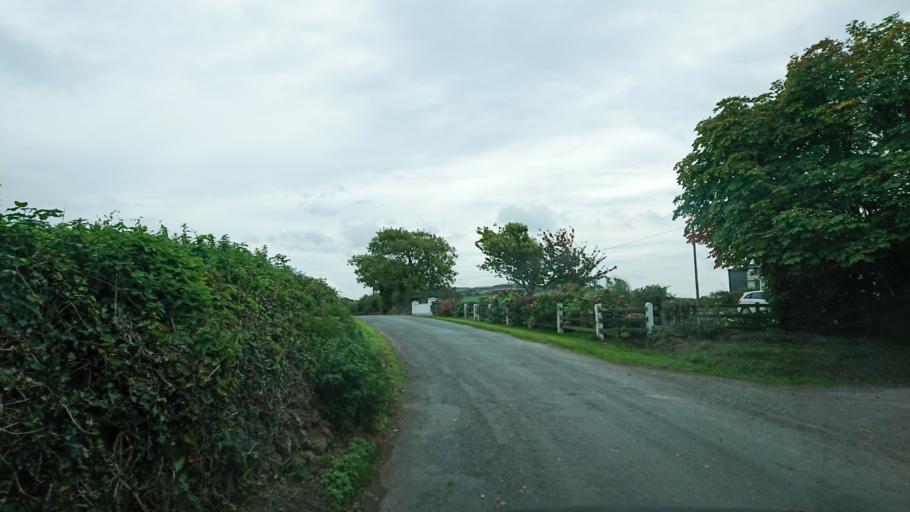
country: IE
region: Munster
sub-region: Waterford
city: Dunmore East
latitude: 52.1796
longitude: -6.9961
